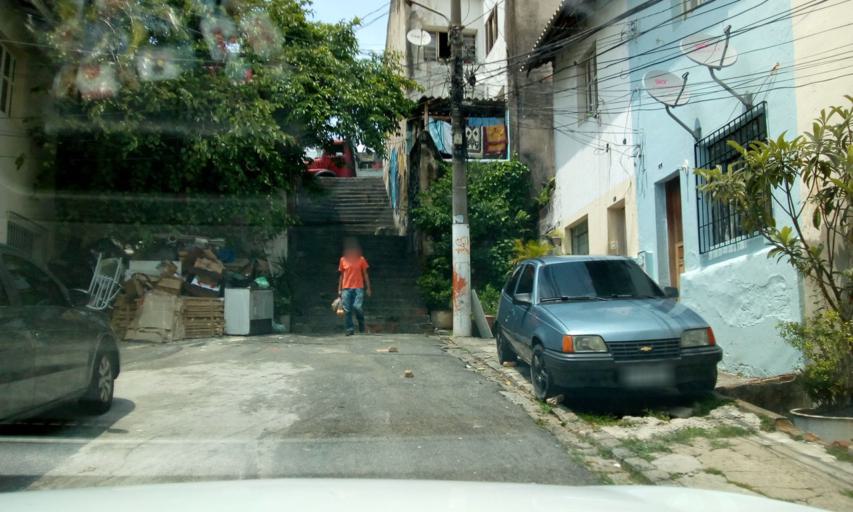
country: BR
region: Sao Paulo
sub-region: Sao Paulo
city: Sao Paulo
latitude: -23.5692
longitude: -46.6293
